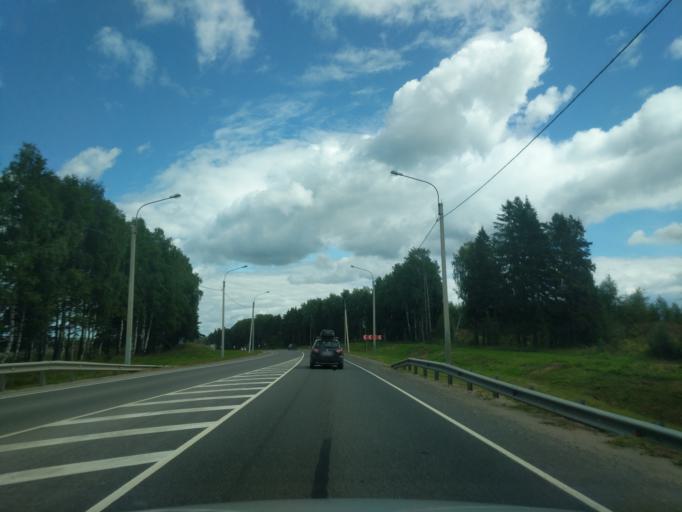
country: RU
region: Jaroslavl
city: Levashevo
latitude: 57.6459
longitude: 40.5413
